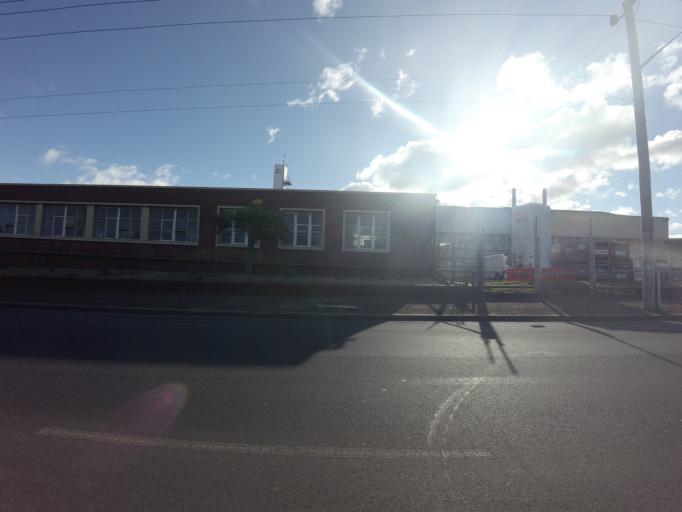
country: AU
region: Tasmania
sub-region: Glenorchy
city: Lutana
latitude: -42.8370
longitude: 147.3210
